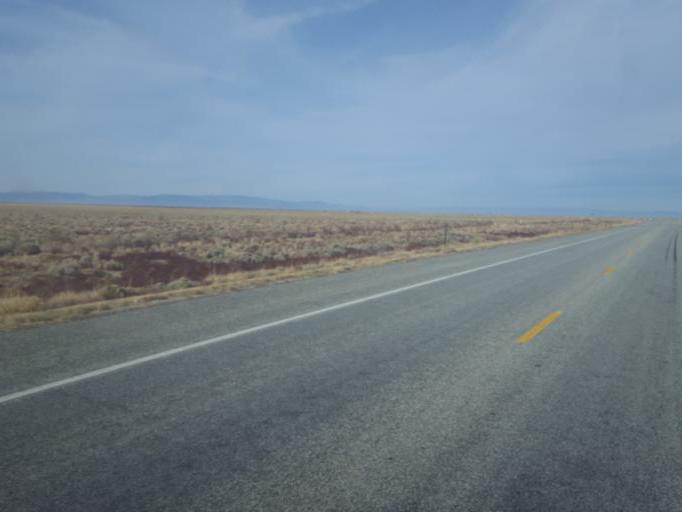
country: US
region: Colorado
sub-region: Alamosa County
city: Alamosa East
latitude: 37.4706
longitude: -105.5766
